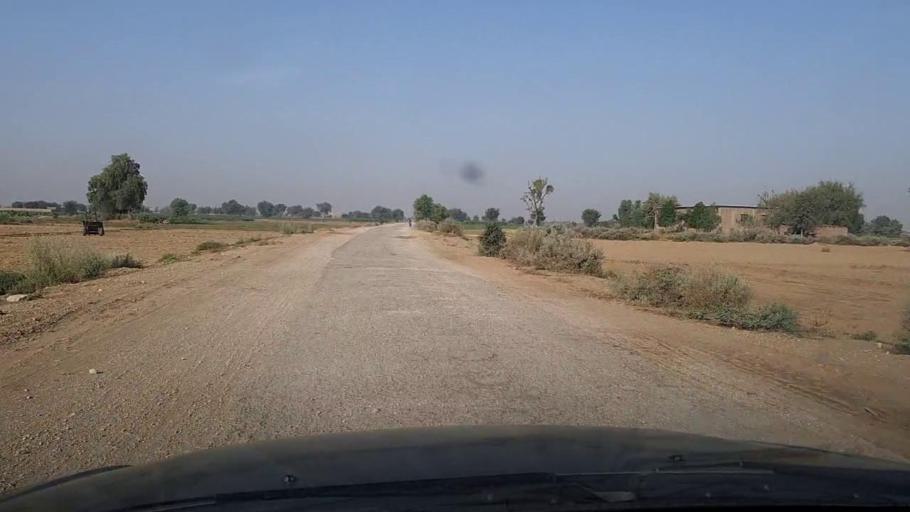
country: PK
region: Sindh
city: Sann
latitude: 26.0293
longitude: 68.1192
